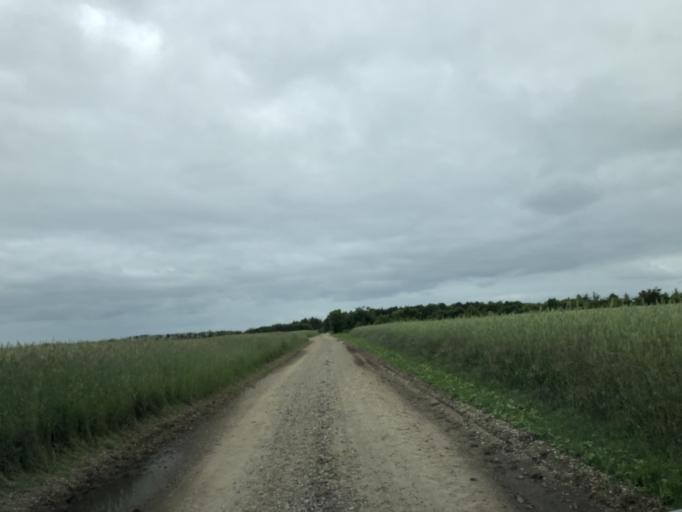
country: DK
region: Central Jutland
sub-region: Holstebro Kommune
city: Ulfborg
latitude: 56.2280
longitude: 8.1766
